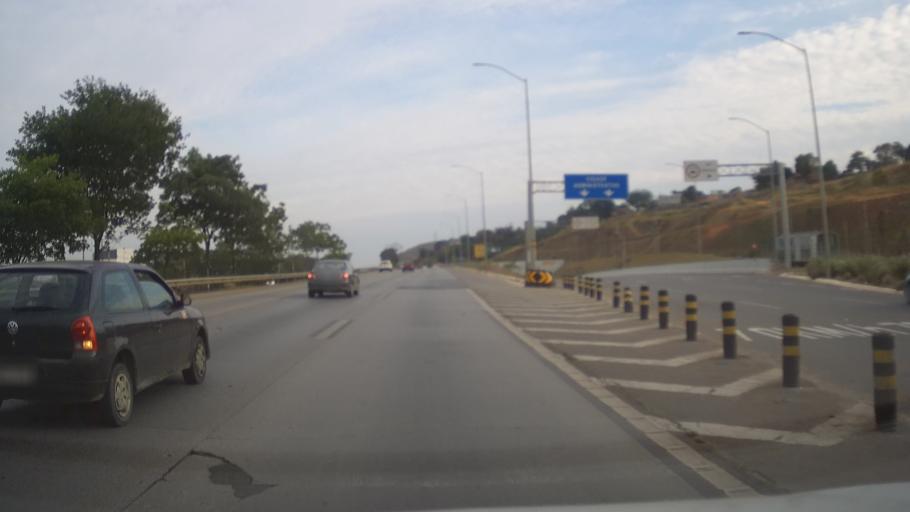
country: BR
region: Minas Gerais
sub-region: Santa Luzia
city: Santa Luzia
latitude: -19.7934
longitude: -43.9493
